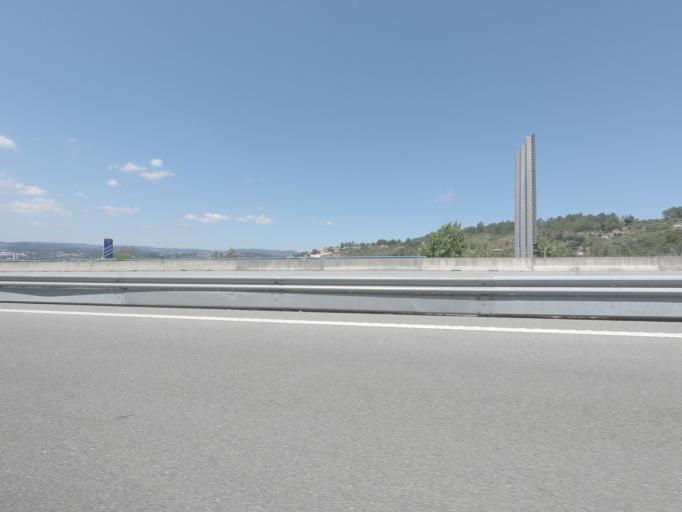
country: PT
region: Porto
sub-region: Amarante
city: Amarante
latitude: 41.2600
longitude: -8.0634
